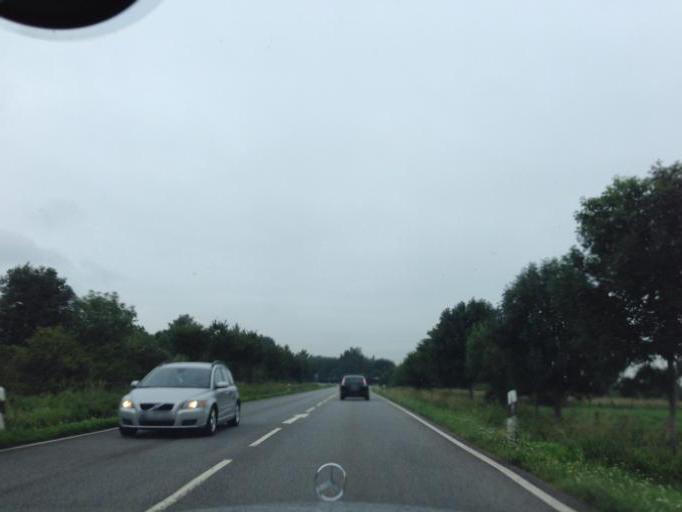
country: DE
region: Schleswig-Holstein
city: Barsbuettel
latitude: 53.5640
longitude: 10.1584
